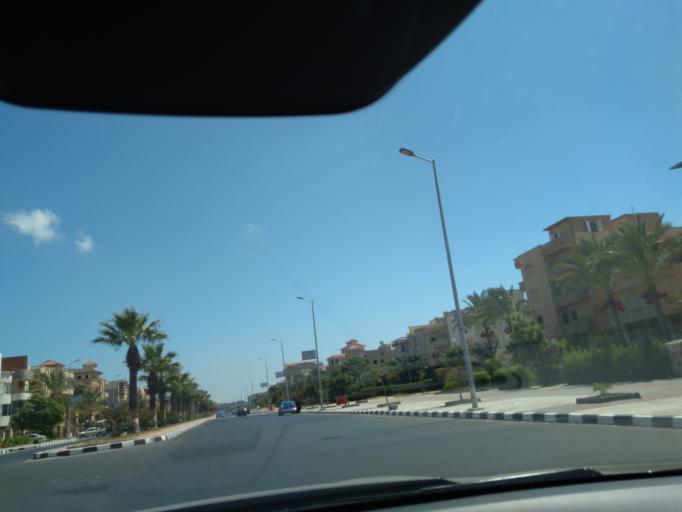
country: EG
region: Dumyat
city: Faraskur
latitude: 31.4323
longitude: 31.6731
